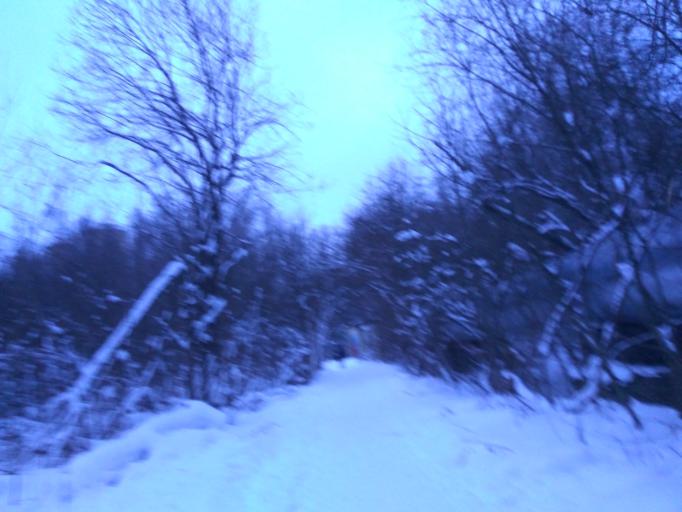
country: RU
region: Moscow
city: Biryulevo
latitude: 55.5886
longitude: 37.6973
